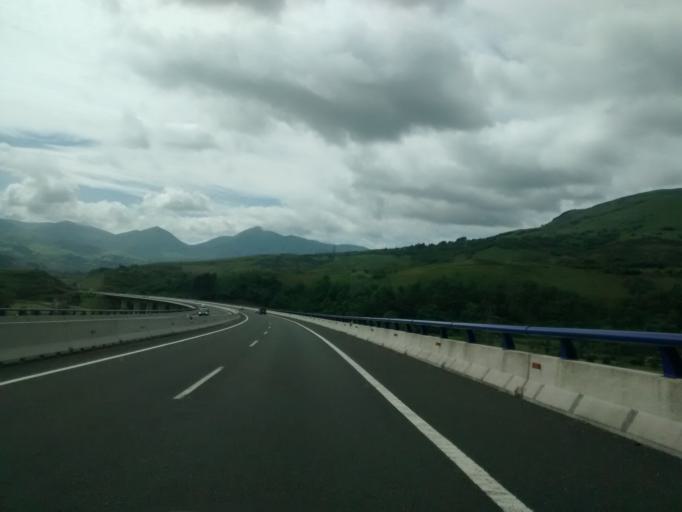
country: ES
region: Cantabria
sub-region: Provincia de Cantabria
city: Arenas de Iguna
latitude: 43.1953
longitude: -4.0714
